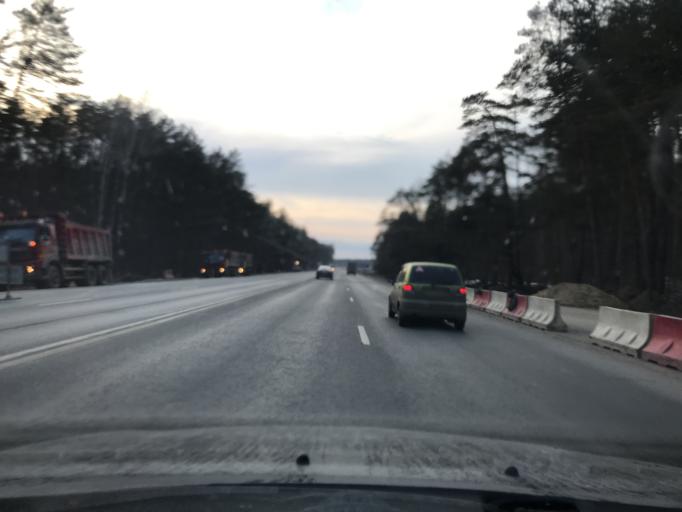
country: RU
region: Kaluga
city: Mstikhino
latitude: 54.5799
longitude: 36.0903
